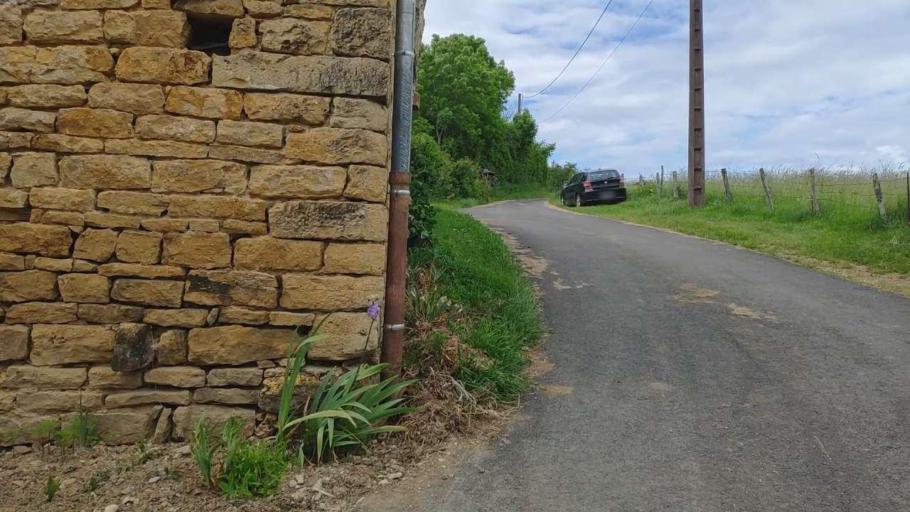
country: FR
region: Franche-Comte
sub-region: Departement du Jura
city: Perrigny
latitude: 46.7796
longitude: 5.5742
